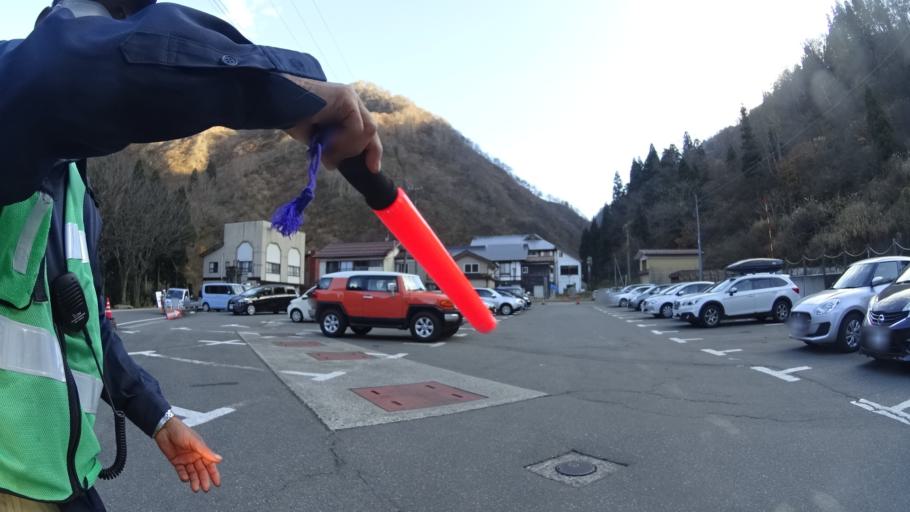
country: JP
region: Niigata
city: Shiozawa
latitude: 36.9746
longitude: 138.7490
